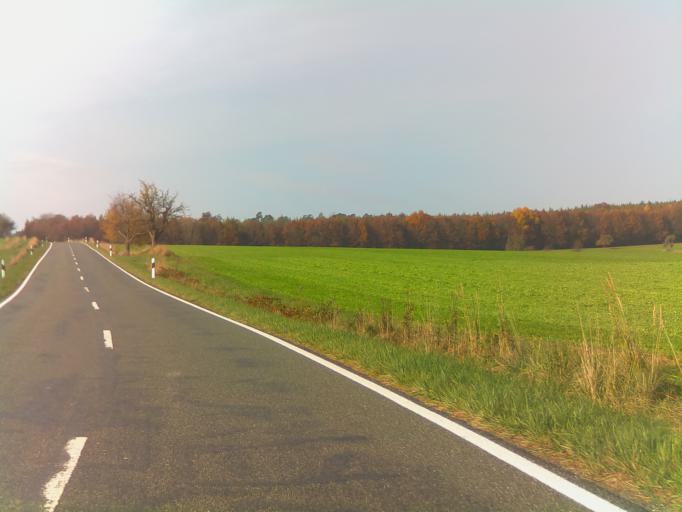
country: DE
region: Bavaria
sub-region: Regierungsbezirk Unterfranken
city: Oberthulba
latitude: 50.2381
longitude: 9.9595
